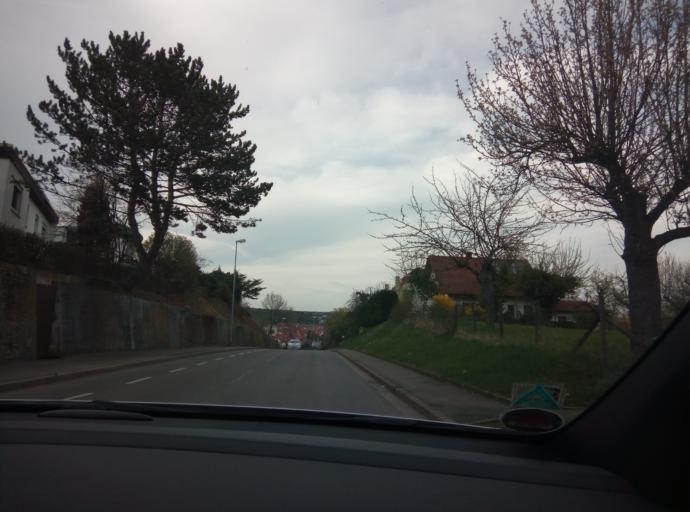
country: DE
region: Baden-Wuerttemberg
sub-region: Tuebingen Region
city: Rottenburg
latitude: 48.4672
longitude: 8.9361
